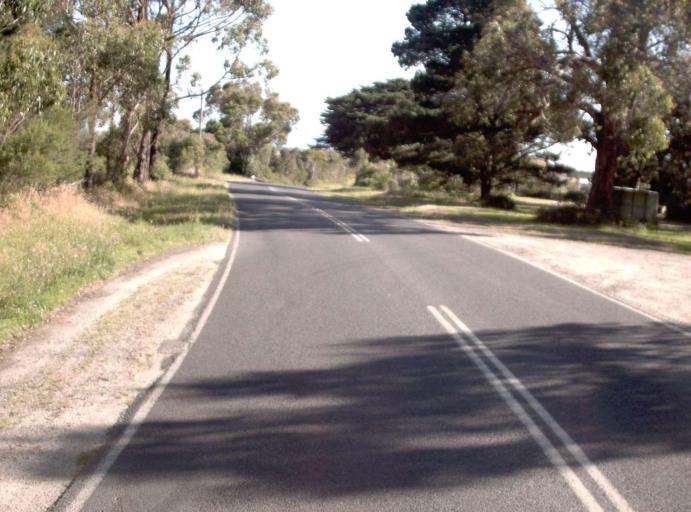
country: AU
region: Victoria
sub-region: Latrobe
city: Morwell
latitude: -38.6710
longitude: 146.3957
